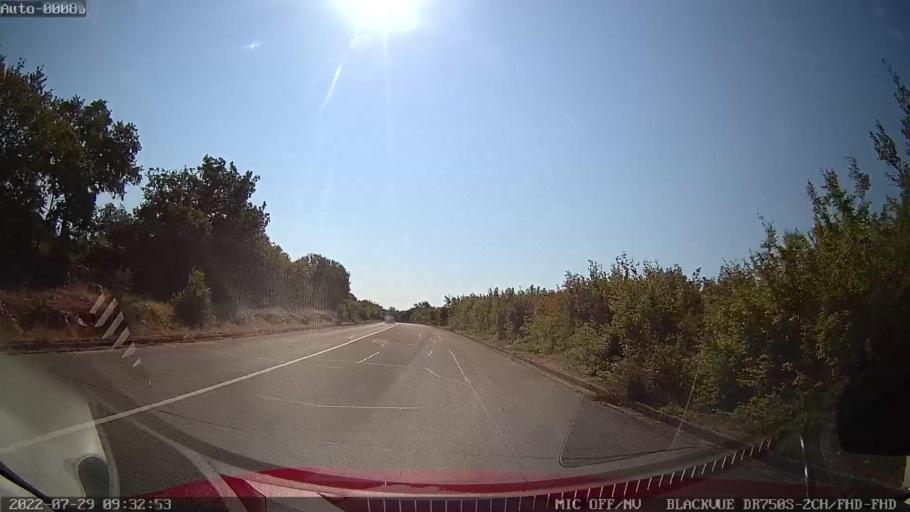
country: HR
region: Zadarska
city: Obrovac
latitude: 44.1806
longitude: 15.7183
